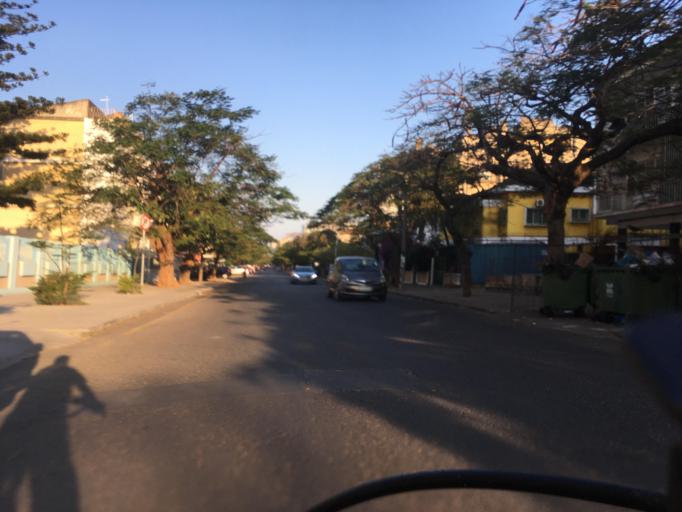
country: MZ
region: Maputo City
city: Maputo
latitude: -25.9714
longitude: 32.5863
